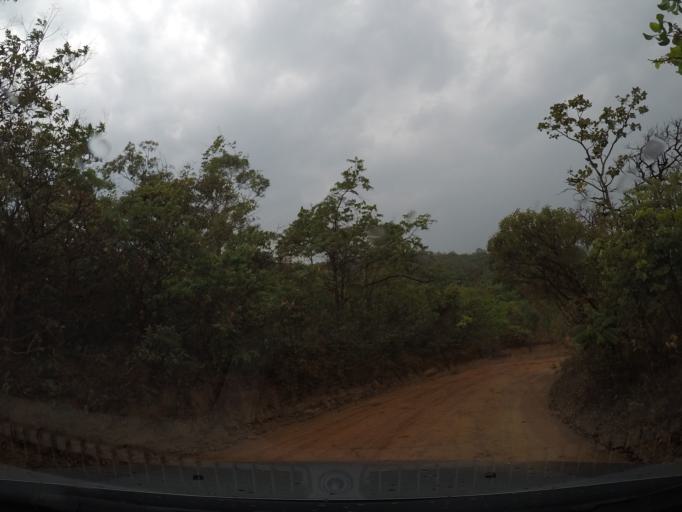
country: BR
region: Goias
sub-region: Pirenopolis
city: Pirenopolis
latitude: -15.8339
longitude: -48.9098
